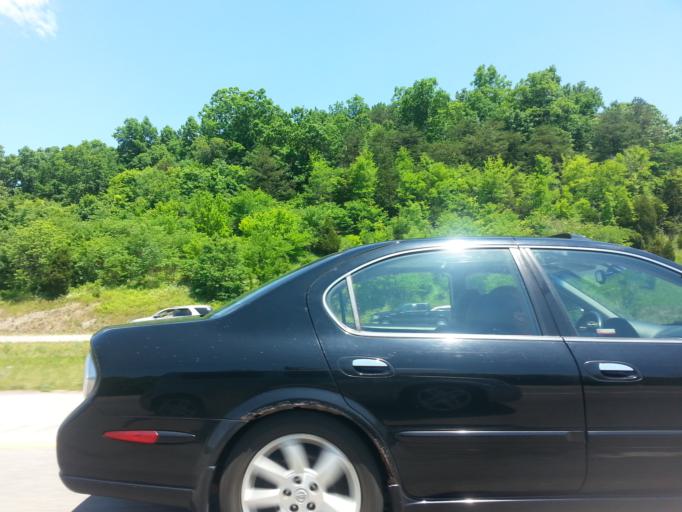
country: US
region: Tennessee
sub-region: Knox County
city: Mascot
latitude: 35.9964
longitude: -83.6928
